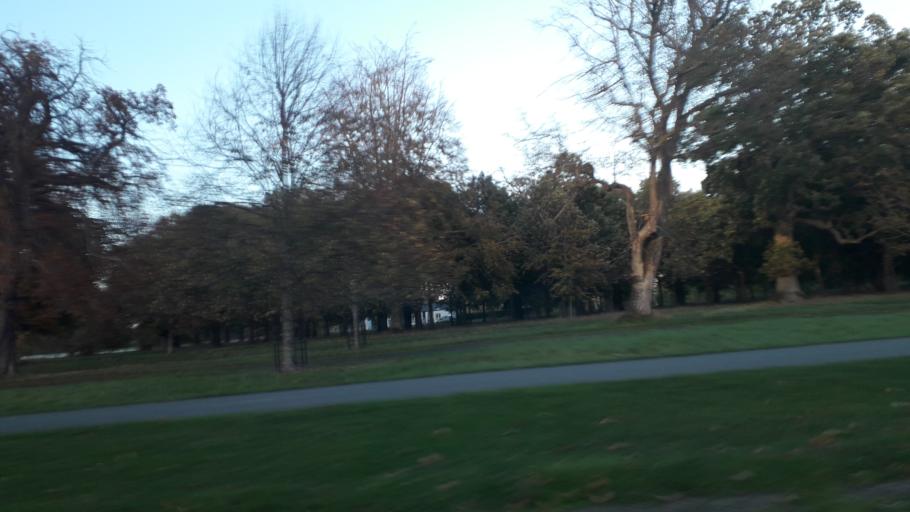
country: IE
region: Leinster
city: Chapelizod
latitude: 53.3617
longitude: -6.3295
